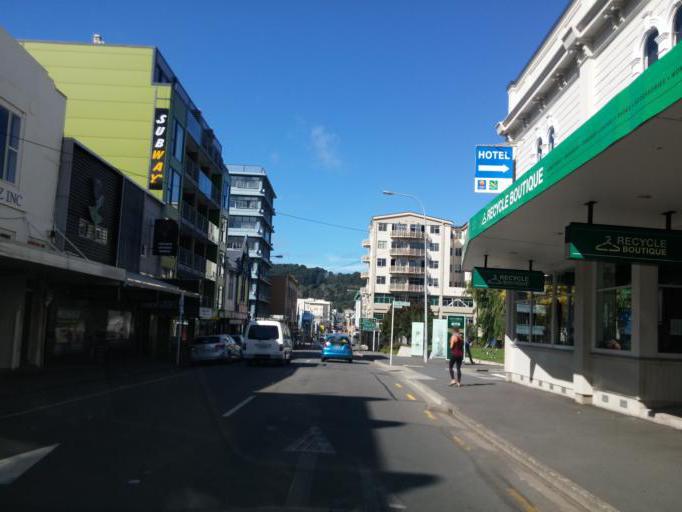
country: NZ
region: Wellington
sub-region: Wellington City
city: Wellington
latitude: -41.2949
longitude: 174.7752
